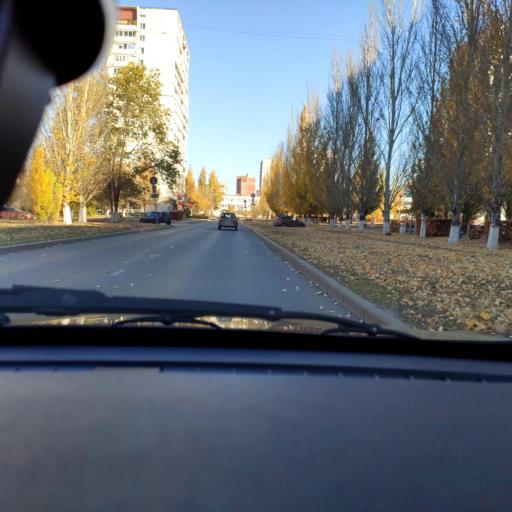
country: RU
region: Samara
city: Tol'yatti
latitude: 53.5354
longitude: 49.3345
